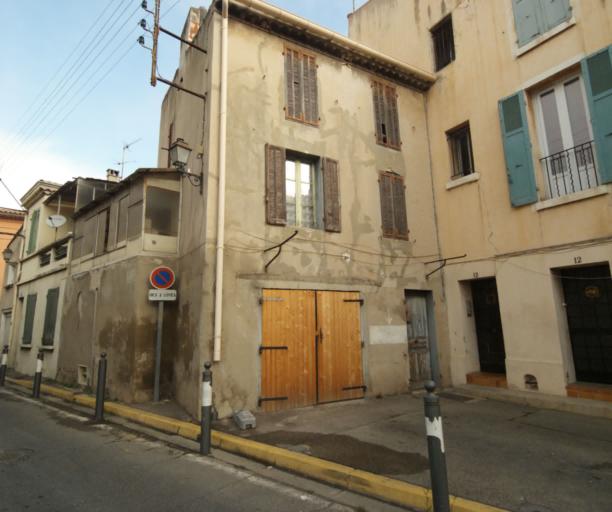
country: FR
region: Provence-Alpes-Cote d'Azur
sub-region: Departement des Bouches-du-Rhone
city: Marignane
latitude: 43.4151
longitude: 5.2140
